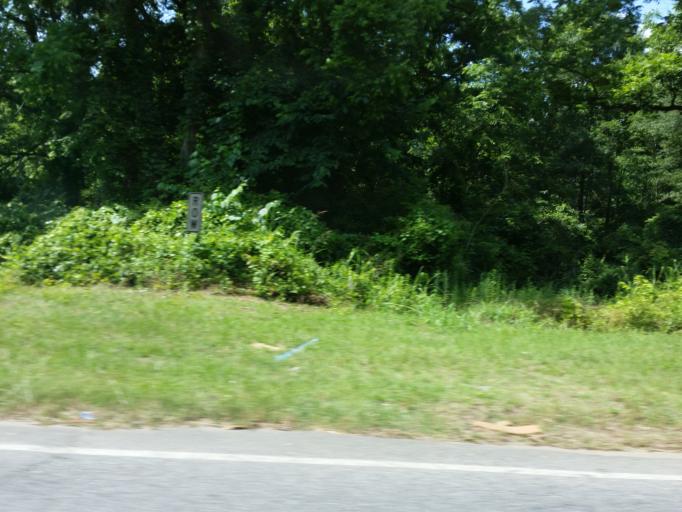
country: US
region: Alabama
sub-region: Greene County
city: Eutaw
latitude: 32.8404
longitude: -87.8804
